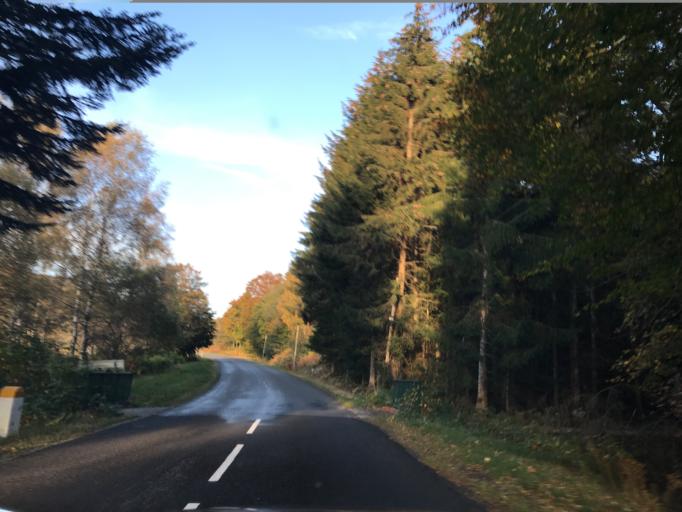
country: FR
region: Rhone-Alpes
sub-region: Departement de la Loire
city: Noiretable
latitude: 45.7891
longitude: 3.6907
